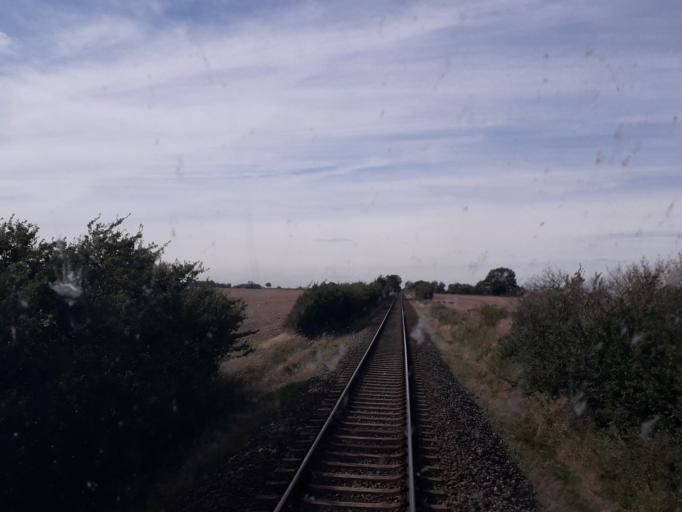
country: DE
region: Brandenburg
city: Neuruppin
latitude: 52.8637
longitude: 12.8844
